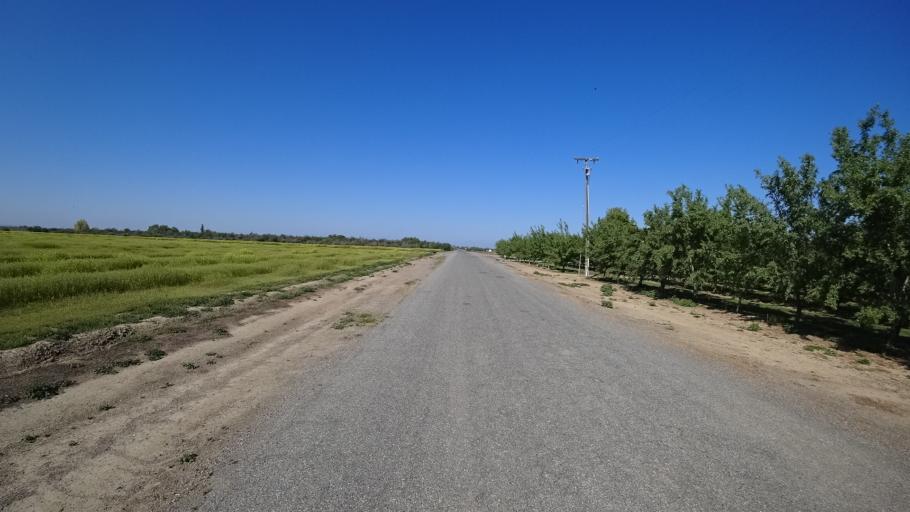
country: US
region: California
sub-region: Glenn County
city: Hamilton City
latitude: 39.6377
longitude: -122.0121
